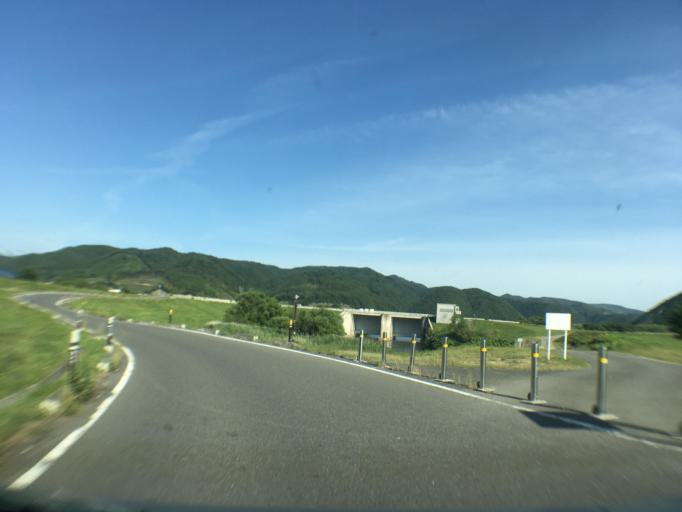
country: JP
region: Miyagi
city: Wakuya
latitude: 38.6079
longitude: 141.2923
